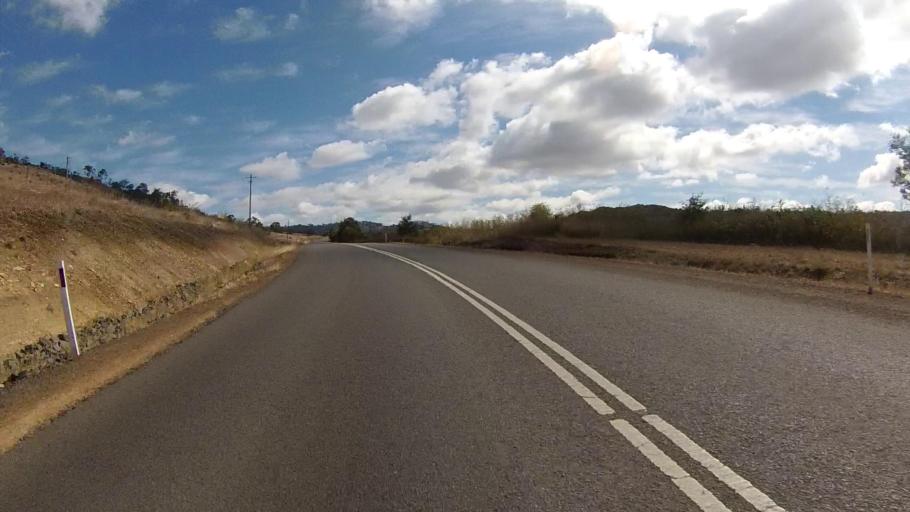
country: AU
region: Tasmania
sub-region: Brighton
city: Old Beach
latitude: -42.7408
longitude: 147.2878
